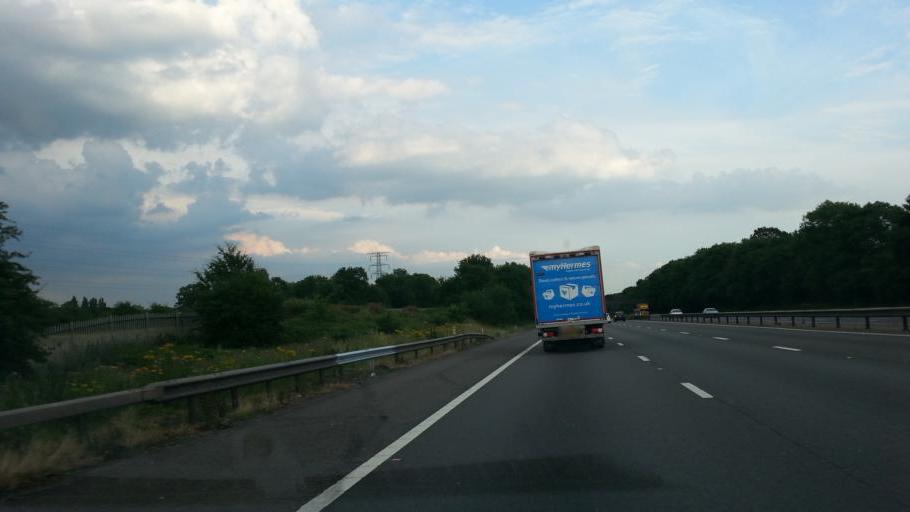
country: GB
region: England
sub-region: Warwickshire
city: Exhall
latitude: 52.4458
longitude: -1.4547
